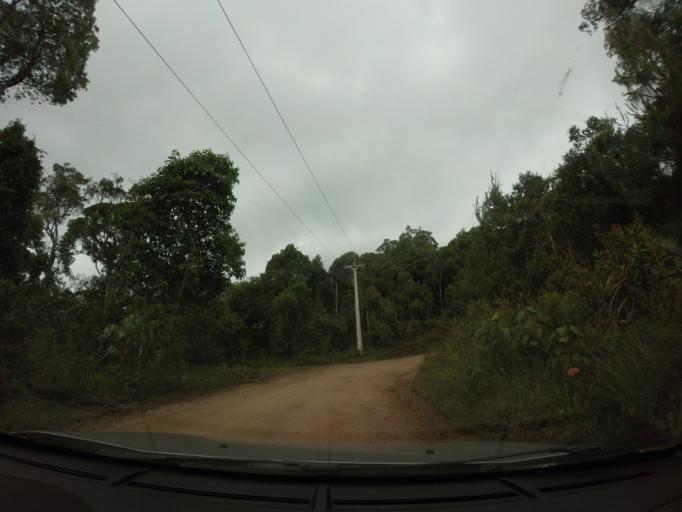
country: BR
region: Sao Paulo
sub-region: Campos Do Jordao
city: Campos do Jordao
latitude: -22.6741
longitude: -45.6242
